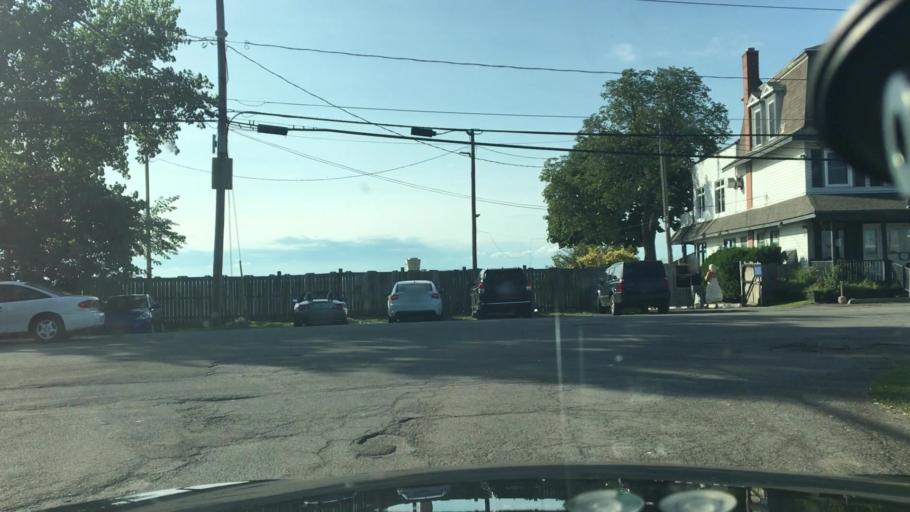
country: US
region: New York
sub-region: Erie County
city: Blasdell
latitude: 42.7815
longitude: -78.8551
